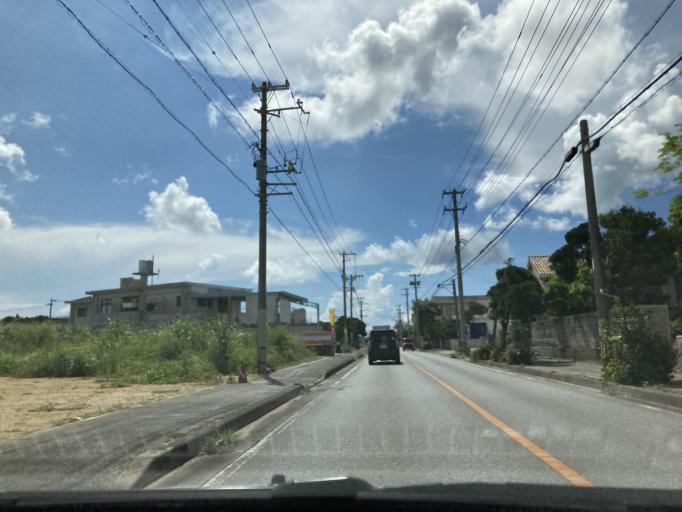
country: JP
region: Okinawa
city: Itoman
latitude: 26.1359
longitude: 127.7303
